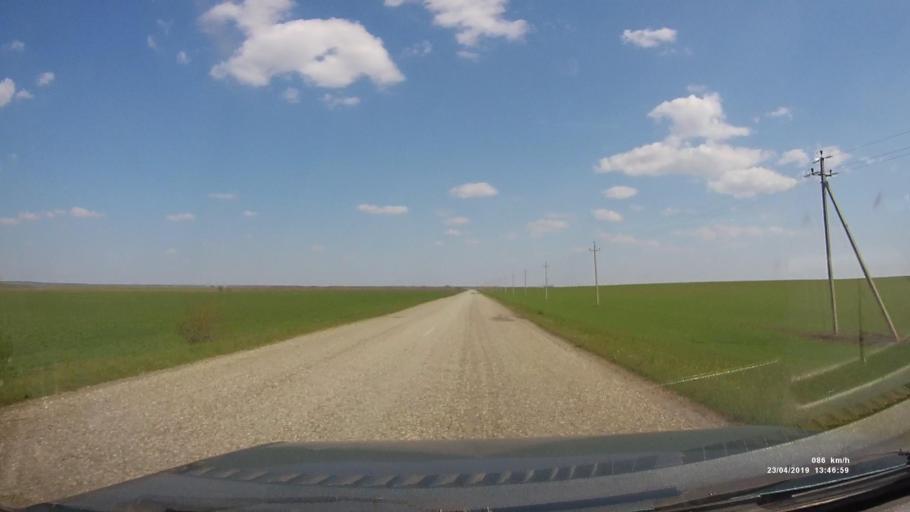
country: RU
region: Kalmykiya
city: Yashalta
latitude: 46.5998
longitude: 42.8452
